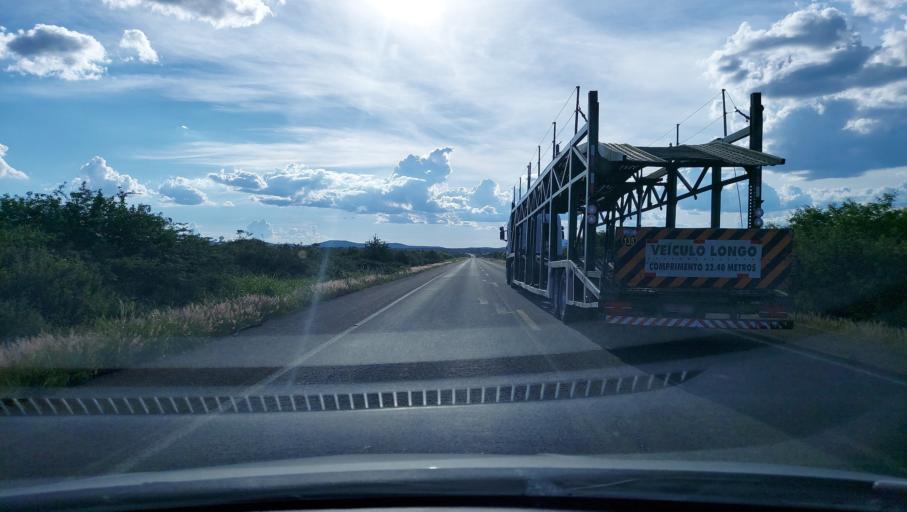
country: BR
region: Bahia
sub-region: Seabra
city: Seabra
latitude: -12.4200
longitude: -42.0926
